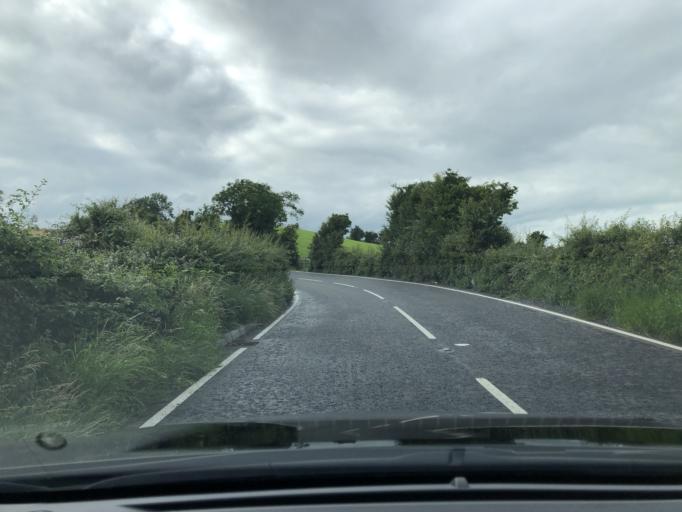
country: GB
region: Northern Ireland
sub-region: Down District
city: Dundrum
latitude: 54.2868
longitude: -5.8283
